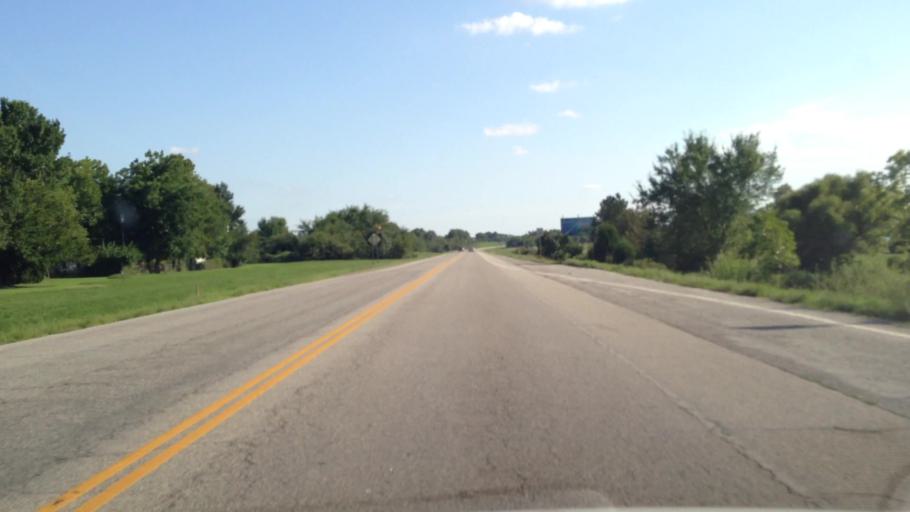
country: US
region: Kansas
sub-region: Crawford County
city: Arma
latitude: 37.5418
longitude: -94.7102
